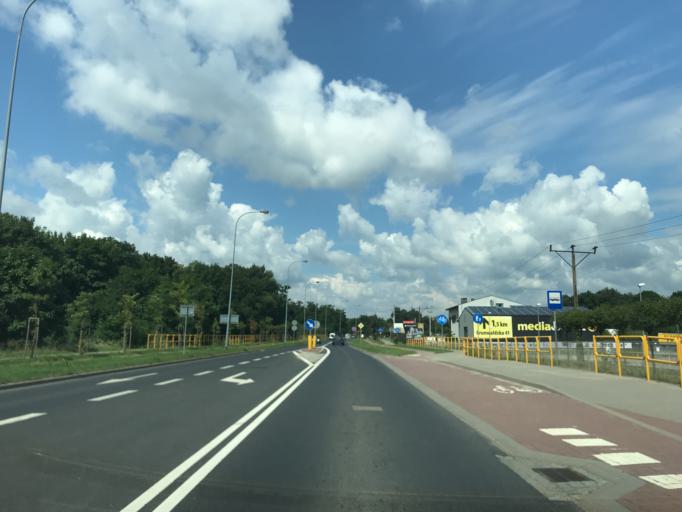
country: PL
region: Warmian-Masurian Voivodeship
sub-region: Powiat ostrodzki
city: Ostroda
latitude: 53.6850
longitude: 19.9911
